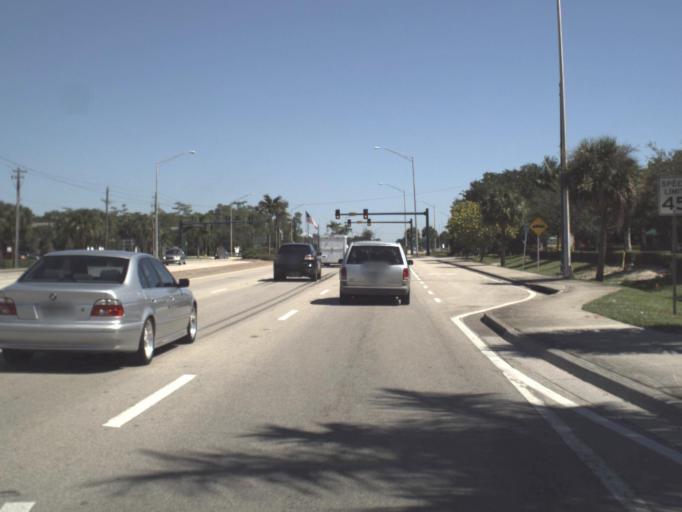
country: US
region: Florida
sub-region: Collier County
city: Vineyards
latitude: 26.2115
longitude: -81.7508
